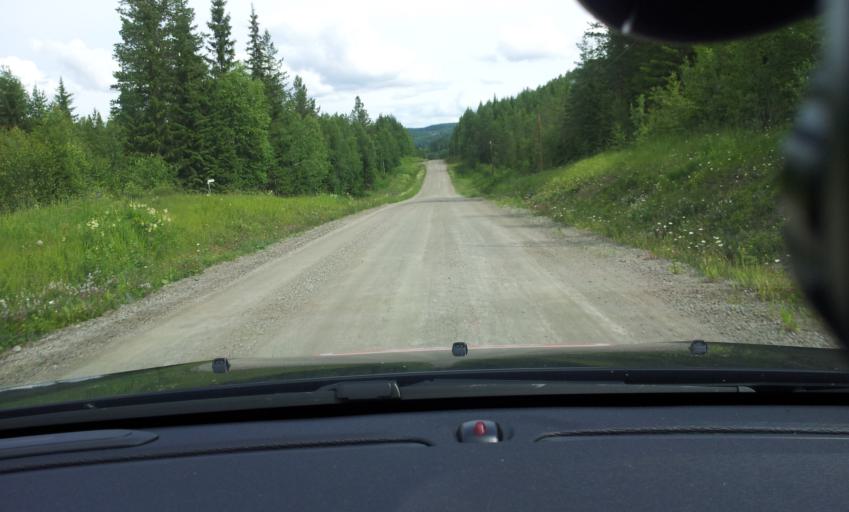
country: SE
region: Jaemtland
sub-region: OEstersunds Kommun
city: Brunflo
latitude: 62.9498
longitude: 14.9902
